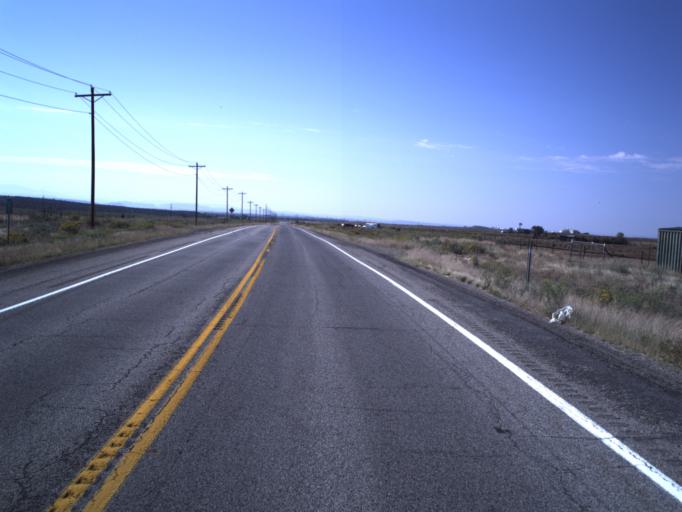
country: US
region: Utah
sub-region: San Juan County
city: Blanding
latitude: 37.5699
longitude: -109.4894
